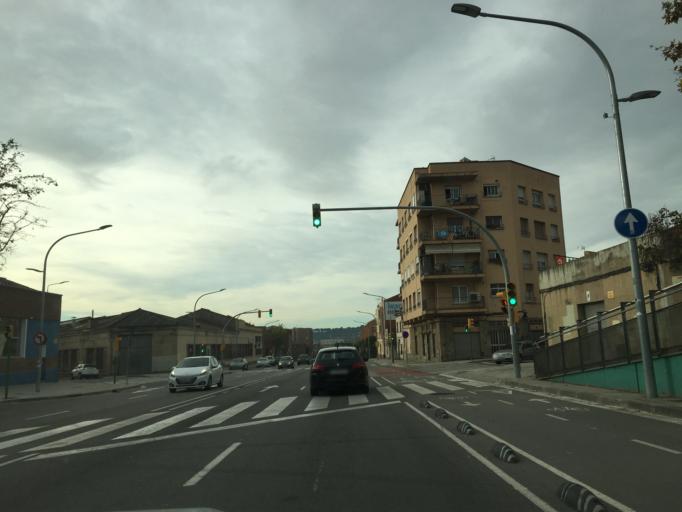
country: ES
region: Catalonia
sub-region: Provincia de Barcelona
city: Sabadell
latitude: 41.5414
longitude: 2.0984
